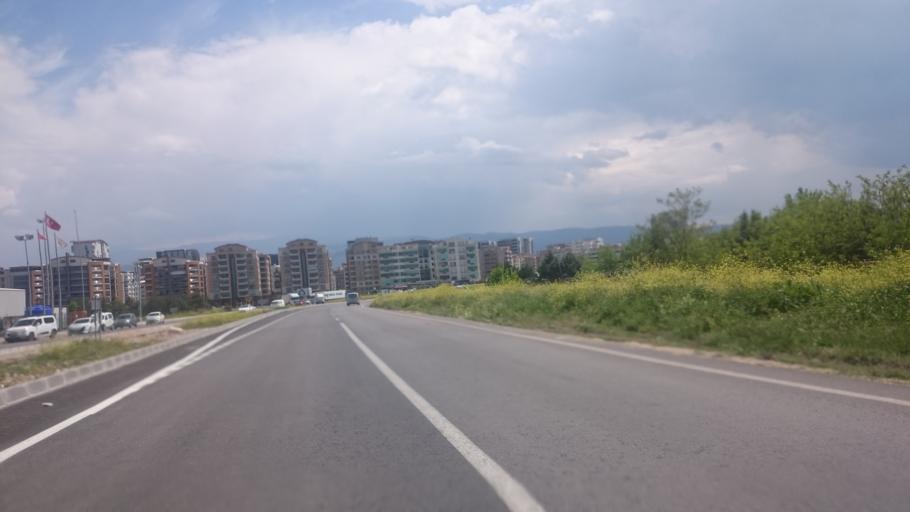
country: TR
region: Bursa
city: Cali
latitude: 40.2255
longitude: 28.9356
